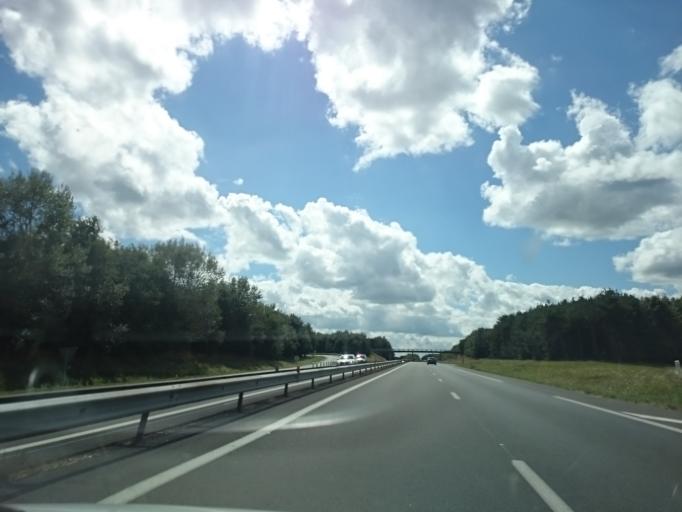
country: FR
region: Pays de la Loire
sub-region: Departement de Maine-et-Loire
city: Durtal
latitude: 47.6688
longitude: -0.2629
